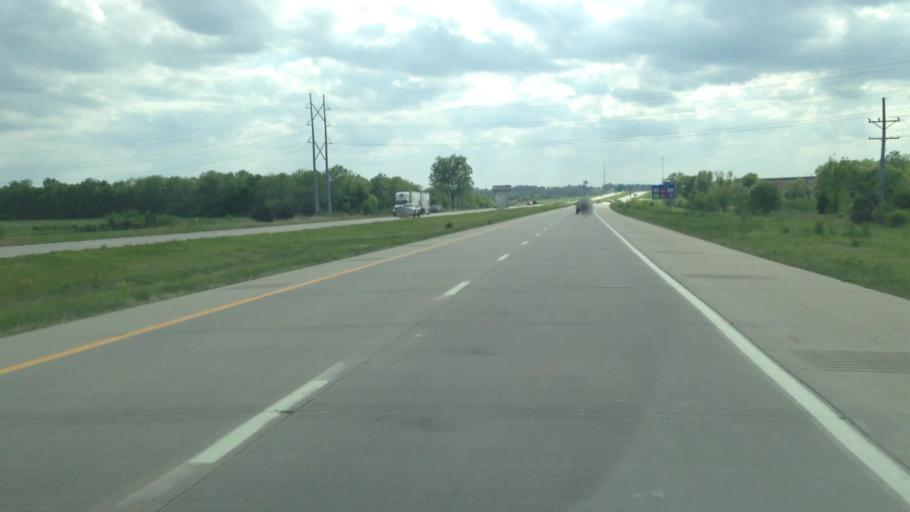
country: US
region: Kansas
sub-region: Franklin County
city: Ottawa
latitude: 38.5794
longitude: -95.2561
